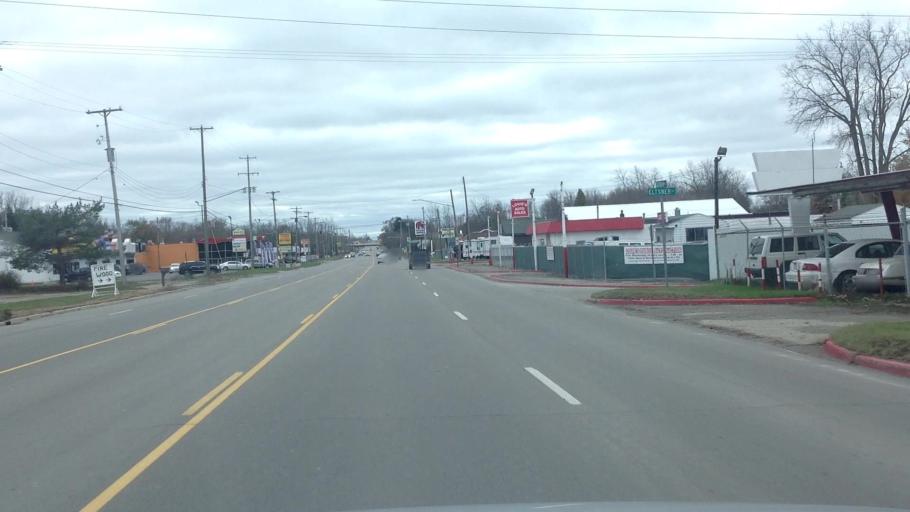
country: US
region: Michigan
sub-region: Genesee County
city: Mount Morris
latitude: 43.1092
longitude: -83.6944
